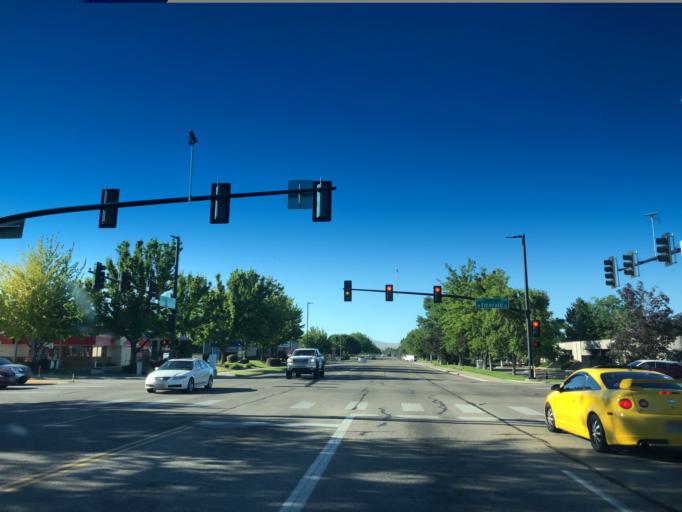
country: US
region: Idaho
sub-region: Ada County
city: Garden City
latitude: 43.6109
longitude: -116.2841
